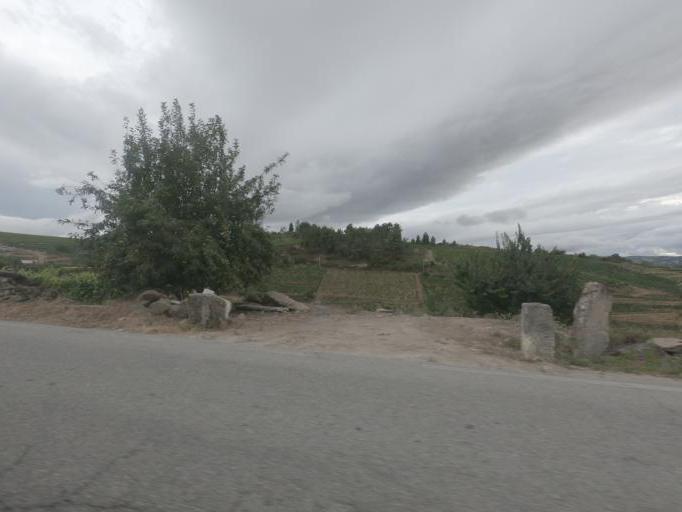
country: PT
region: Vila Real
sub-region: Sabrosa
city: Sabrosa
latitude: 41.2866
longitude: -7.5137
